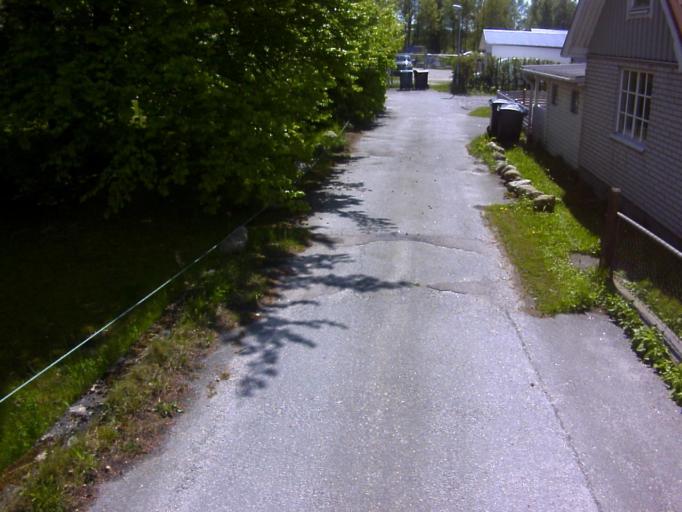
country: SE
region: Blekinge
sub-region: Solvesborgs Kommun
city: Soelvesborg
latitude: 56.0606
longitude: 14.6138
